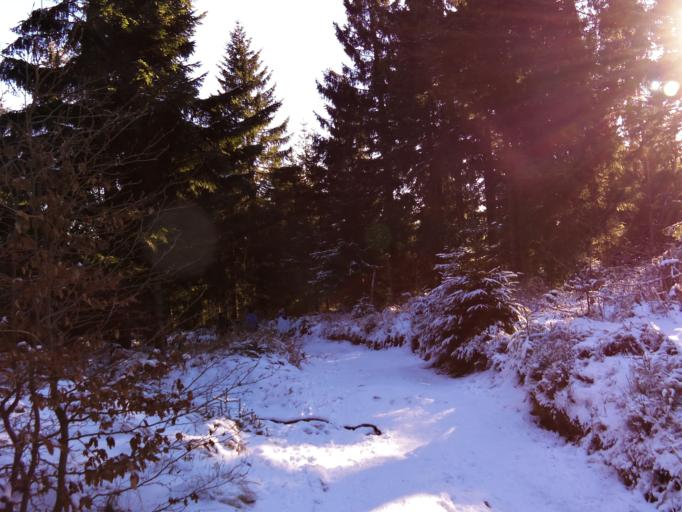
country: DE
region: Bavaria
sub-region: Upper Franconia
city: Bischofsgrun
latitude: 50.0288
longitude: 11.8174
